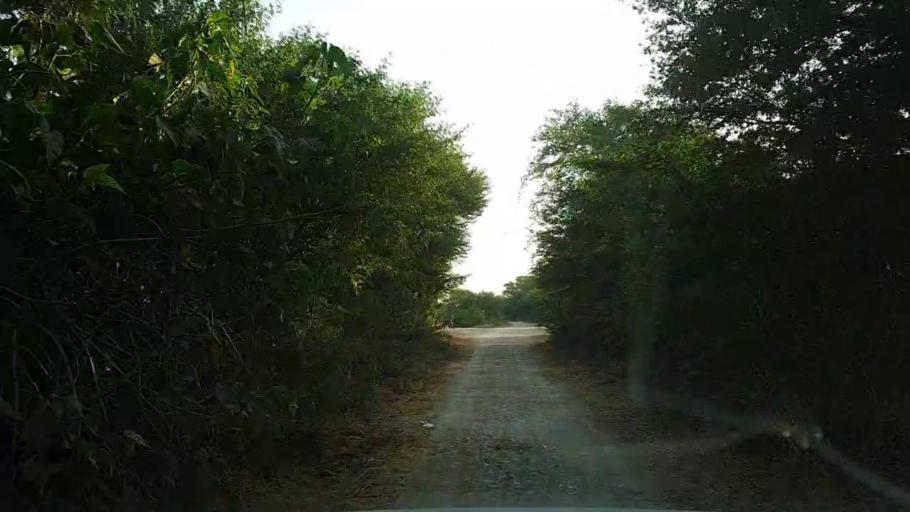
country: PK
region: Sindh
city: Daro Mehar
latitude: 24.7618
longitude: 68.1916
